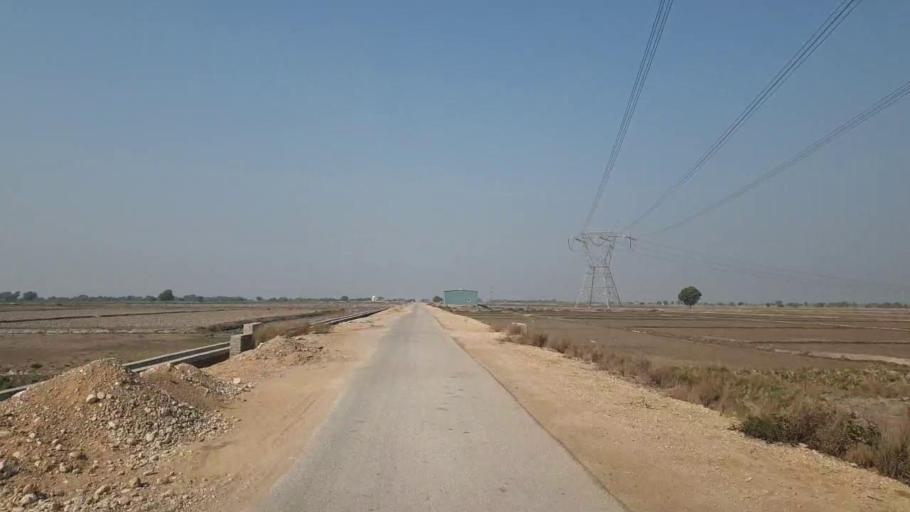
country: PK
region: Sindh
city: Sehwan
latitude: 26.4290
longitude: 67.7670
